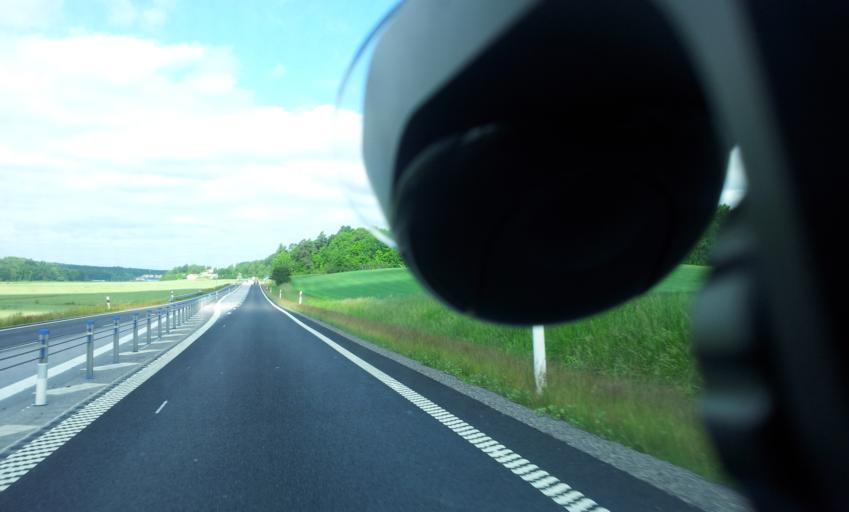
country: SE
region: OEstergoetland
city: Lindo
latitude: 58.5466
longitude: 16.2628
